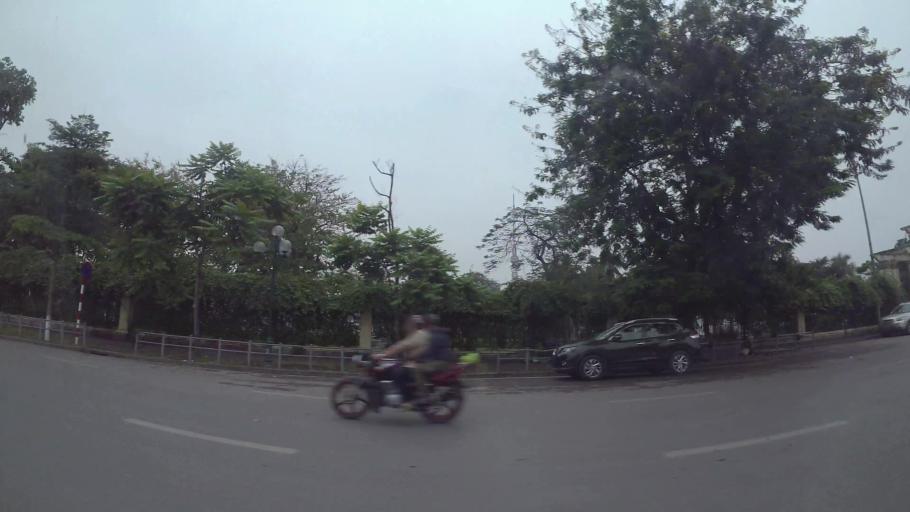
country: VN
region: Ha Noi
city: Hai BaTrung
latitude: 21.0114
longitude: 105.8414
